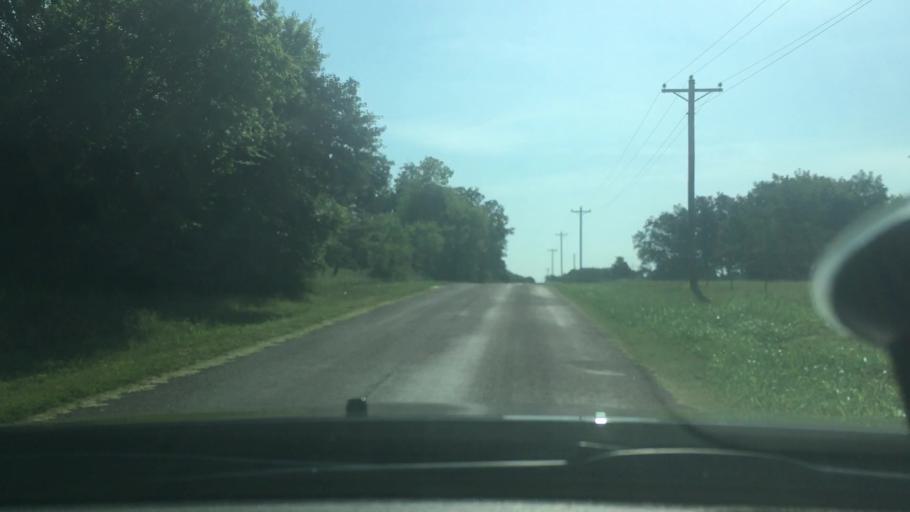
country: US
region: Oklahoma
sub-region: Garvin County
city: Pauls Valley
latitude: 34.6521
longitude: -97.3607
